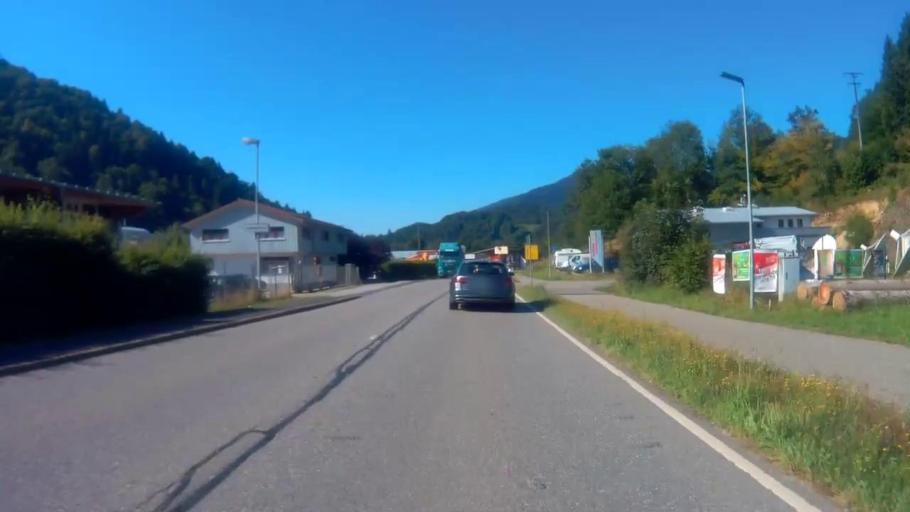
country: DE
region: Baden-Wuerttemberg
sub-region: Freiburg Region
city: Wembach
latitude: 47.7755
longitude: 7.8909
